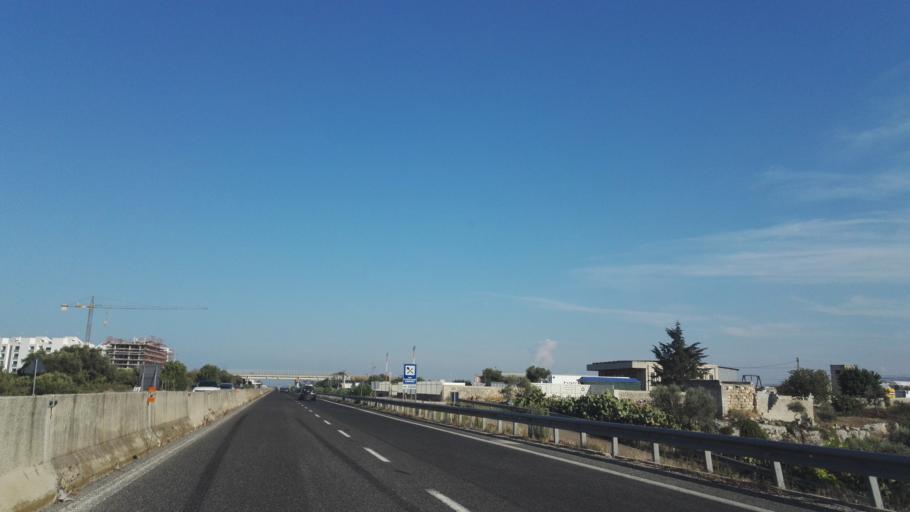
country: IT
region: Apulia
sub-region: Provincia di Bari
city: Monopoli
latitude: 40.9335
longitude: 17.2966
